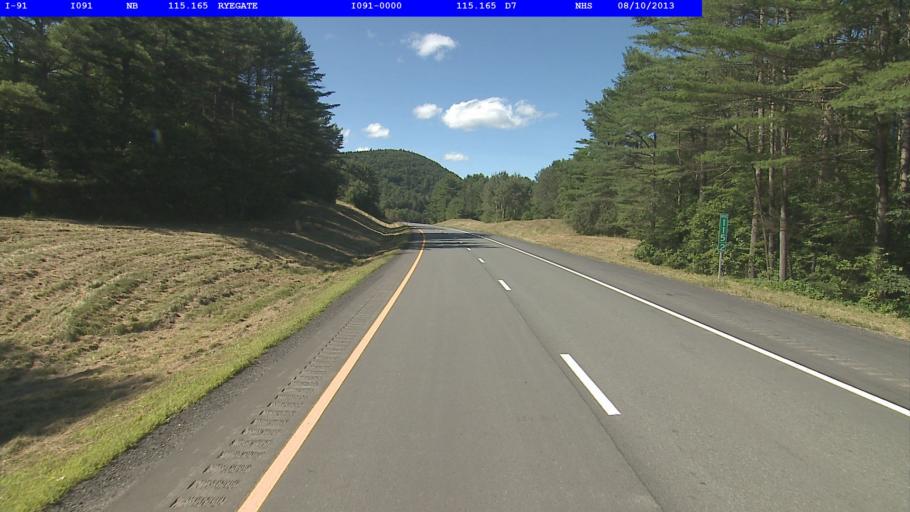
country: US
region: New Hampshire
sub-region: Grafton County
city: Woodsville
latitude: 44.2272
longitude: -72.0673
